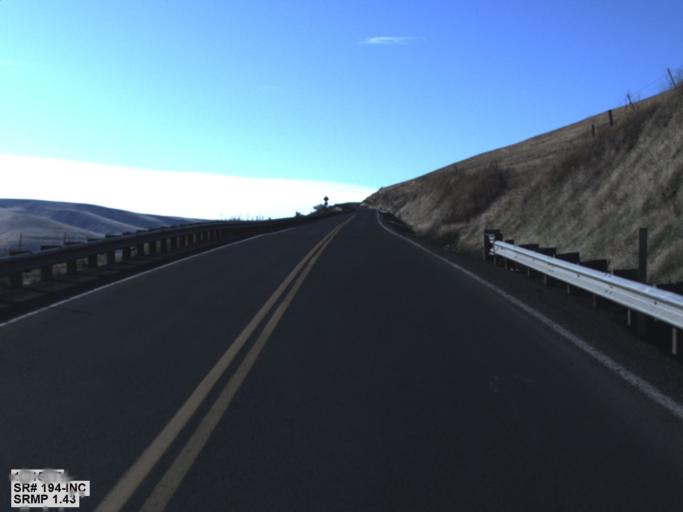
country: US
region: Washington
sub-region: Whitman County
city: Colfax
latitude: 46.7203
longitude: -117.4664
